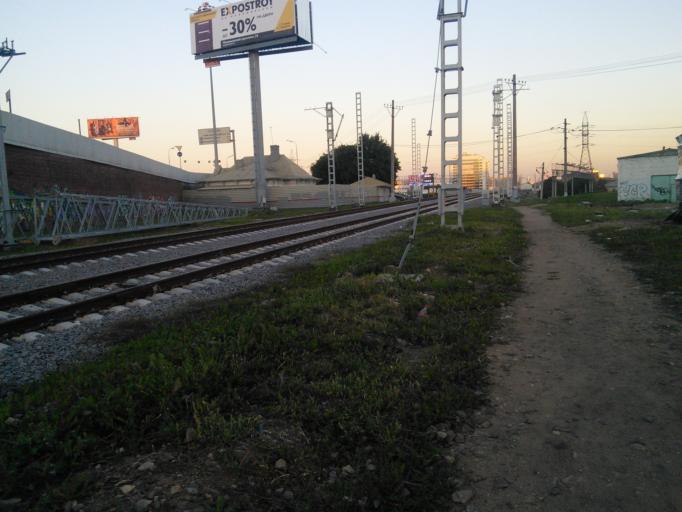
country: RU
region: Moskovskaya
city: Presnenskiy
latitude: 55.7371
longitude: 37.5370
